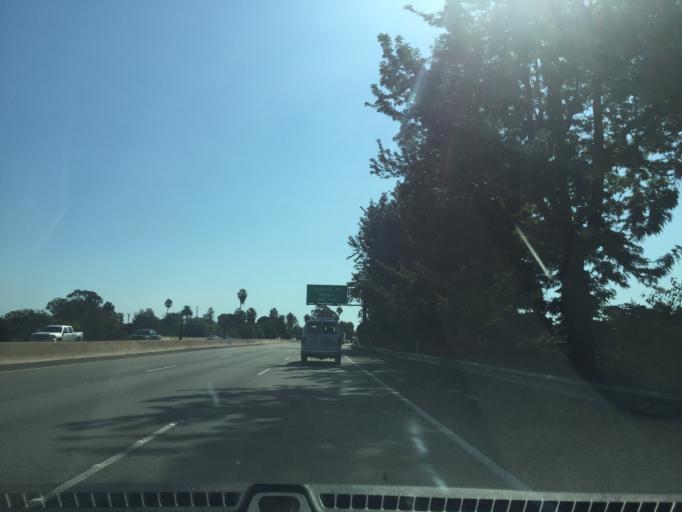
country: US
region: California
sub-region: Santa Barbara County
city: Santa Barbara
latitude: 34.4170
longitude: -119.7086
